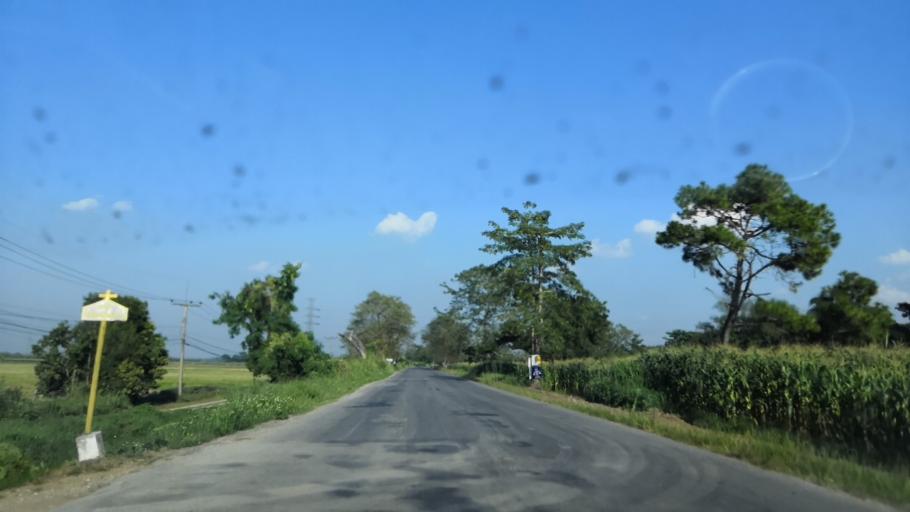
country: TH
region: Chiang Rai
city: Wiang Chai
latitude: 19.9469
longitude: 99.9191
